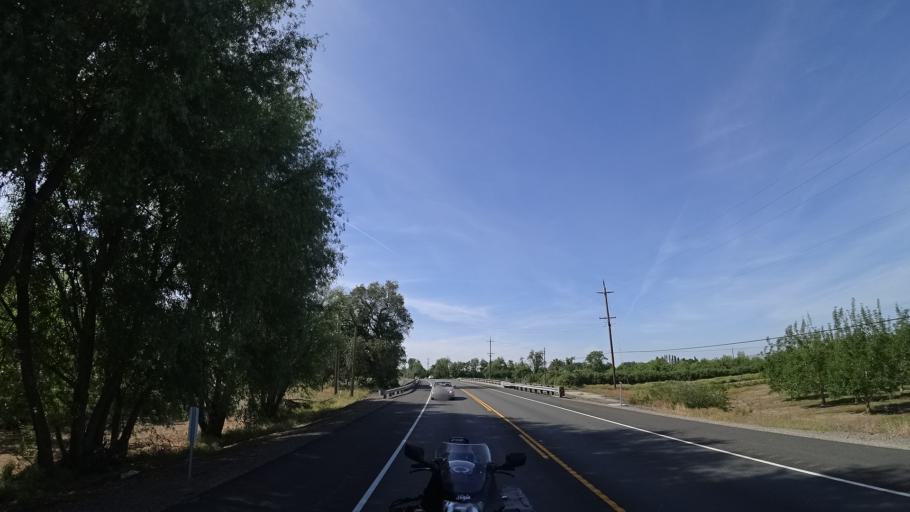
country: US
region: California
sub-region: Glenn County
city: Hamilton City
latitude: 39.8784
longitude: -121.9706
